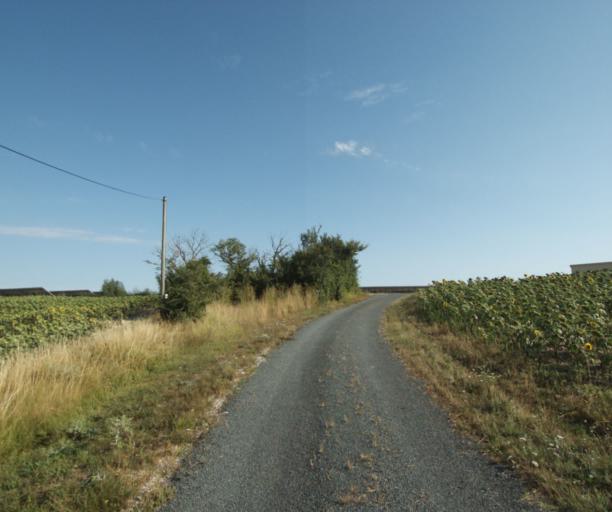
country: FR
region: Midi-Pyrenees
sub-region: Departement de la Haute-Garonne
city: Avignonet-Lauragais
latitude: 43.4412
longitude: 1.8129
